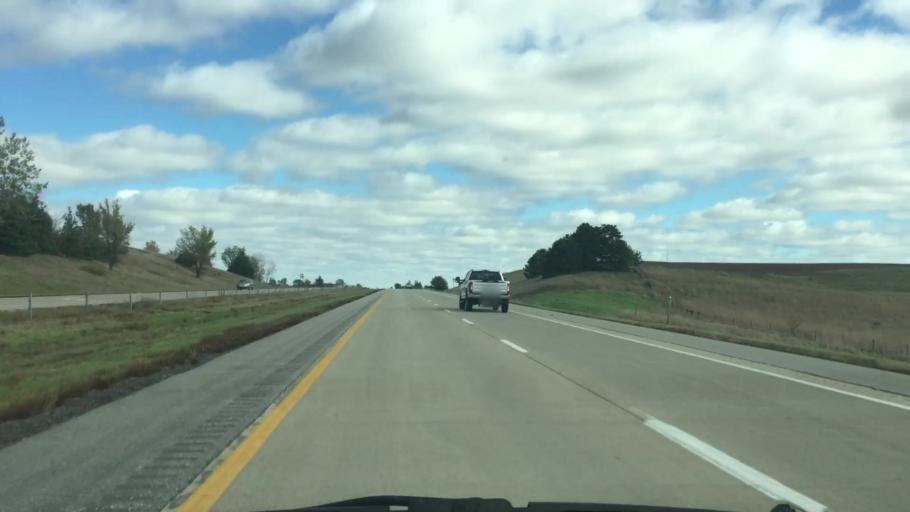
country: US
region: Iowa
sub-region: Poweshiek County
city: Brooklyn
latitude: 41.6959
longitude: -92.3837
